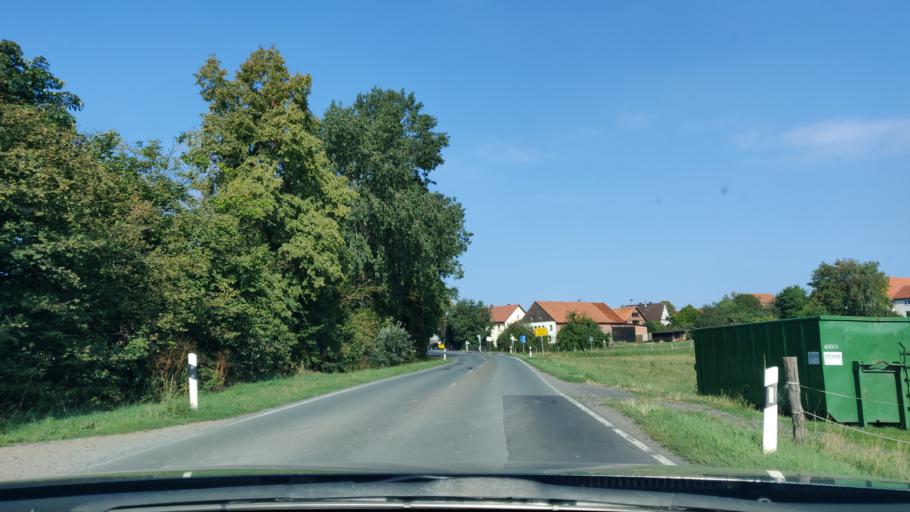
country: DE
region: Hesse
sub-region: Regierungsbezirk Kassel
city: Bad Wildungen
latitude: 51.1425
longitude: 9.1798
